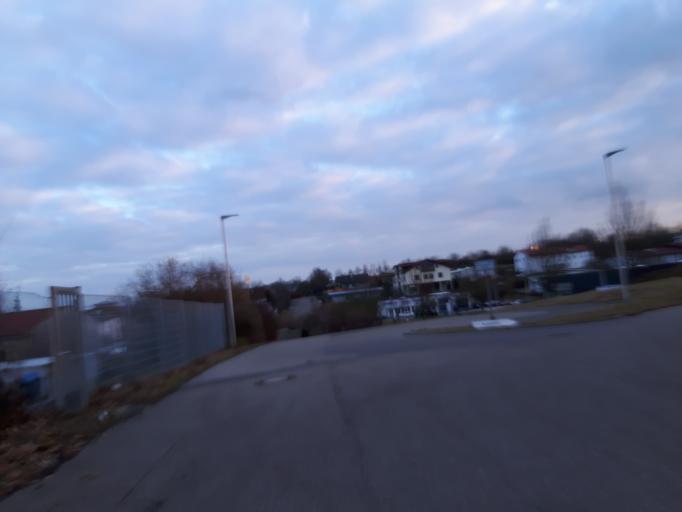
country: DE
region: Baden-Wuerttemberg
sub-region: Regierungsbezirk Stuttgart
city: Ohringen
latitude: 49.1946
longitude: 9.4837
